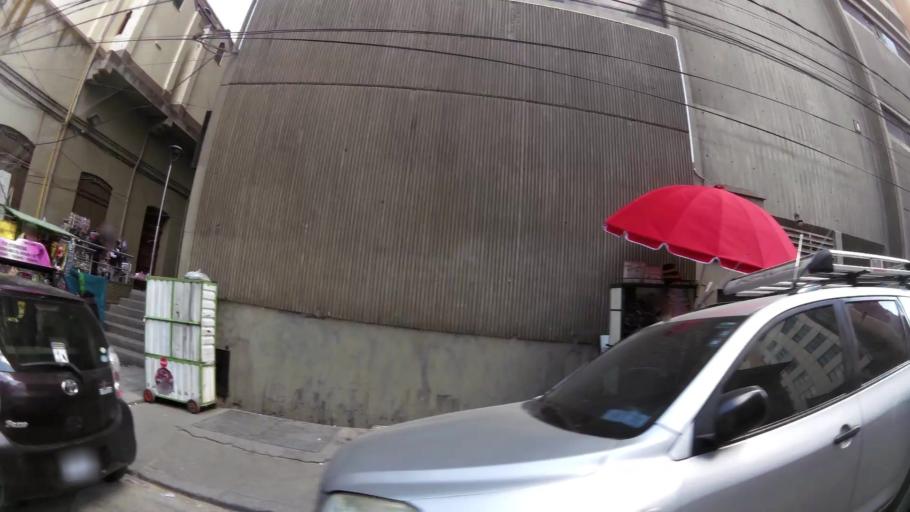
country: BO
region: La Paz
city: La Paz
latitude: -16.5029
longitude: -68.1311
